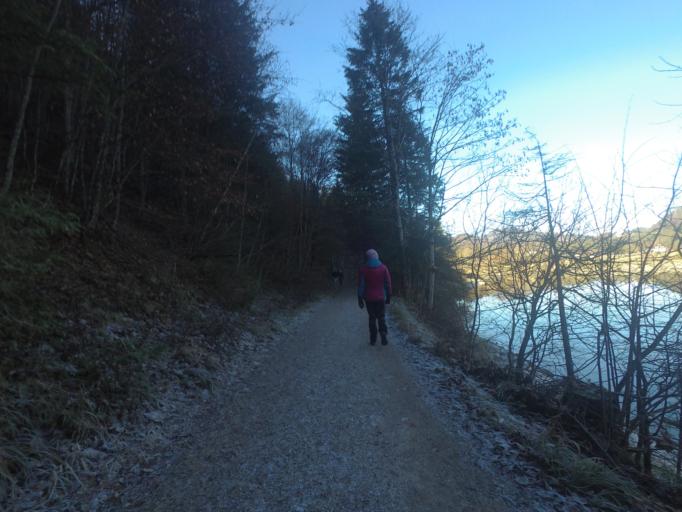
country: AT
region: Salzburg
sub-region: Politischer Bezirk Salzburg-Umgebung
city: Faistenau
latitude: 47.7495
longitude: 13.2418
